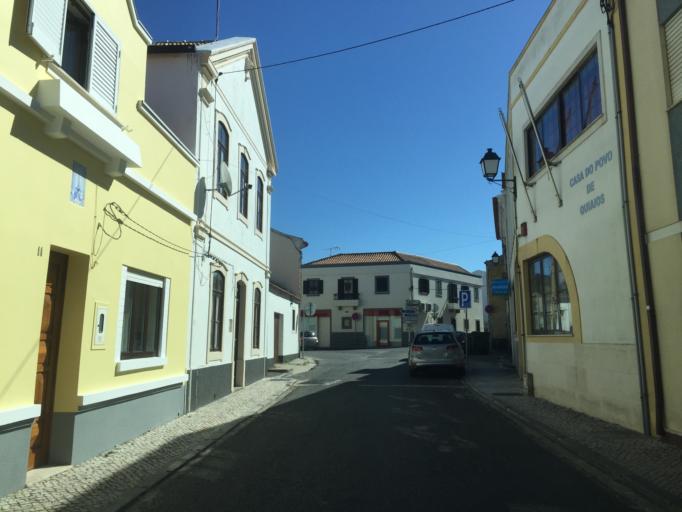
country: PT
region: Coimbra
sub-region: Figueira da Foz
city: Tavarede
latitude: 40.2134
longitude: -8.8508
